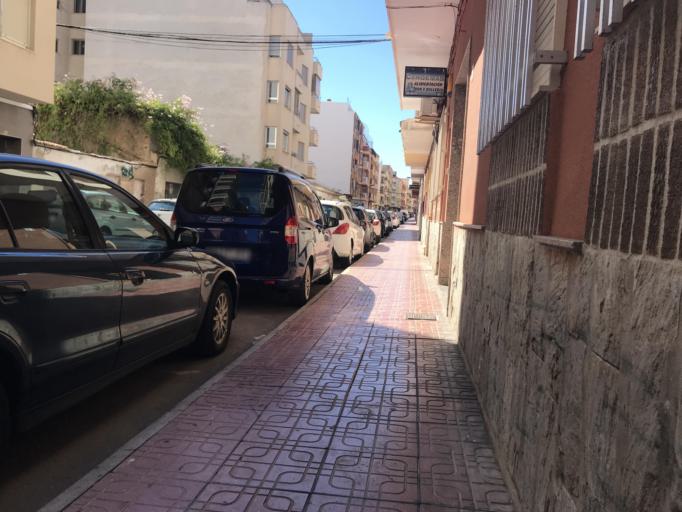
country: ES
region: Valencia
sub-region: Provincia de Alicante
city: Torrevieja
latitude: 37.9766
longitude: -0.6721
